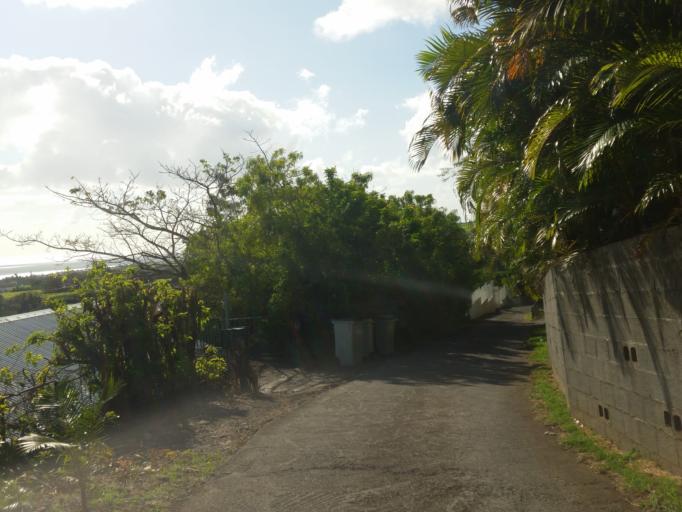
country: RE
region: Reunion
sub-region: Reunion
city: Sainte-Marie
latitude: -20.9163
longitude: 55.5073
